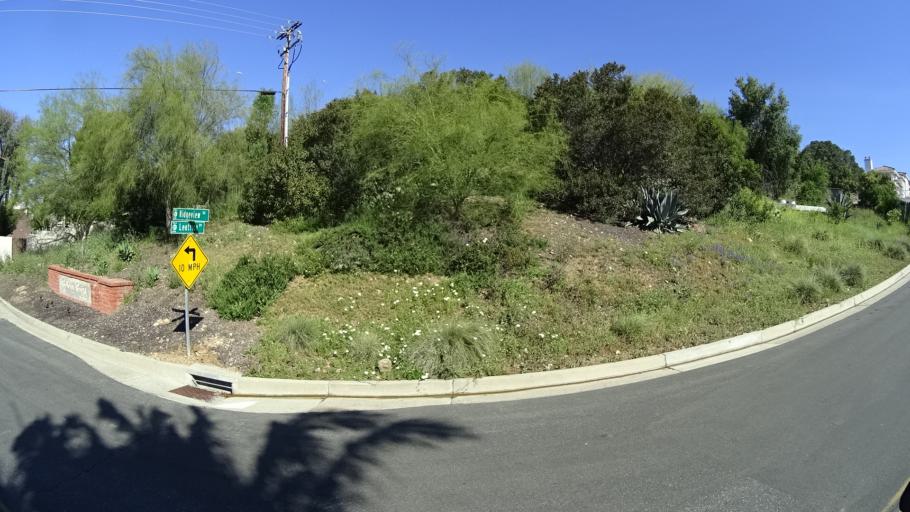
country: US
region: California
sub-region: Orange County
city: Villa Park
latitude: 33.8201
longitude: -117.8007
